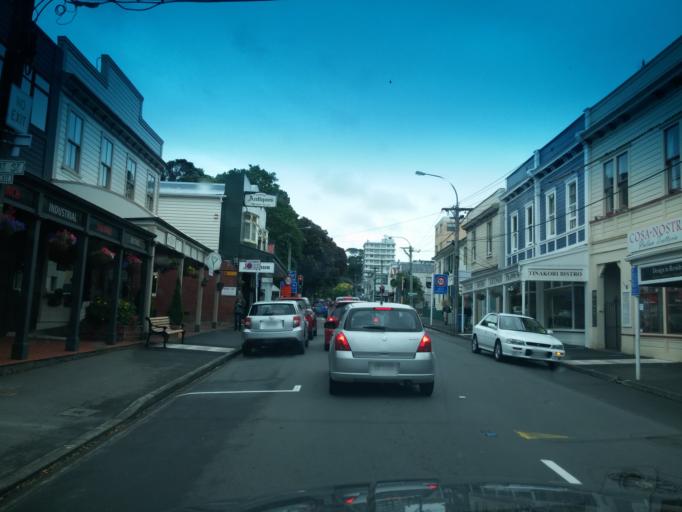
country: NZ
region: Wellington
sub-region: Wellington City
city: Kelburn
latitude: -41.2783
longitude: 174.7699
